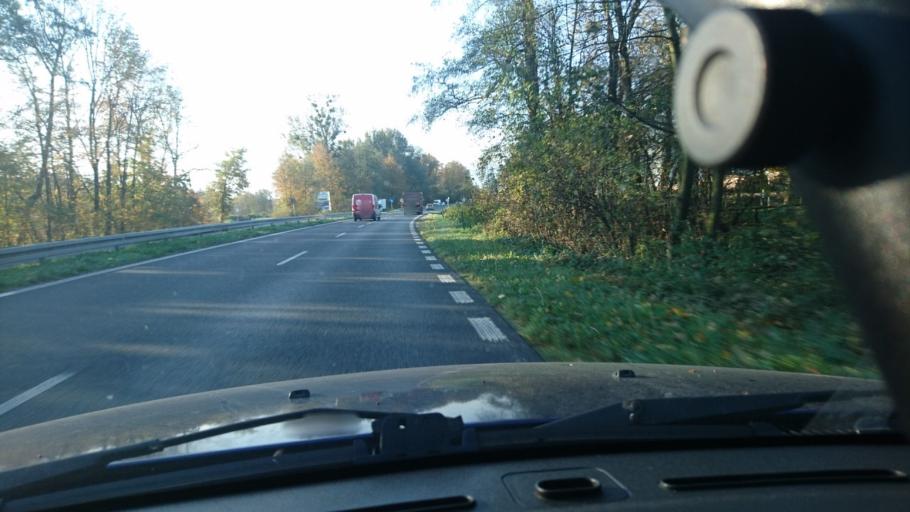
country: PL
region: Silesian Voivodeship
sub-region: Powiat cieszynski
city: Gorki Wielkie
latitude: 49.7641
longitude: 18.8091
